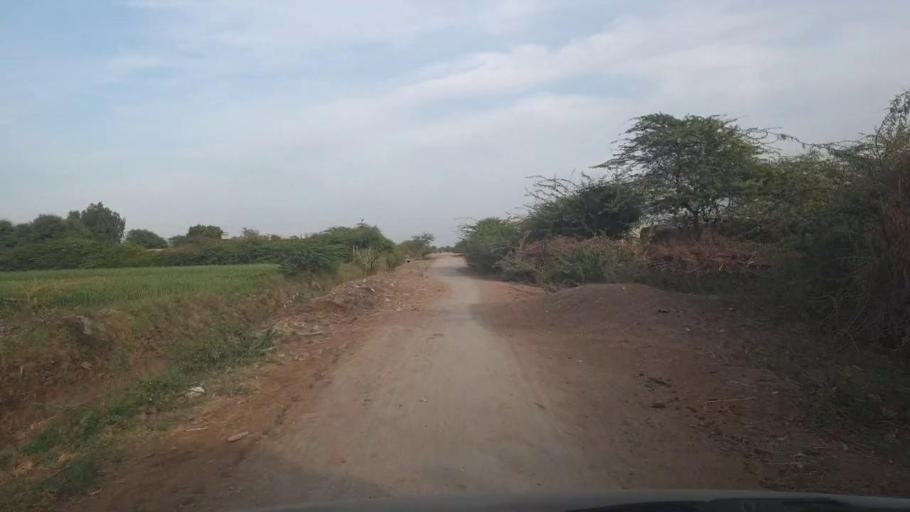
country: PK
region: Sindh
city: Kunri
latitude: 25.2647
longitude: 69.5423
